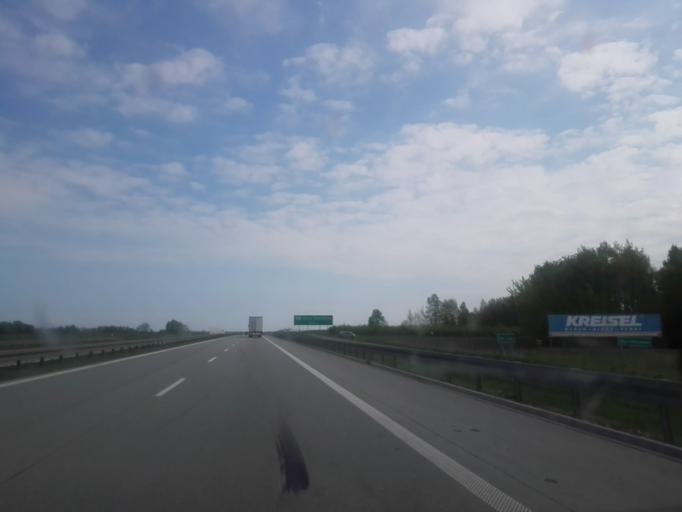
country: PL
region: Lodz Voivodeship
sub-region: Powiat skierniewicki
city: Kowiesy
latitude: 51.9040
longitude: 20.4371
